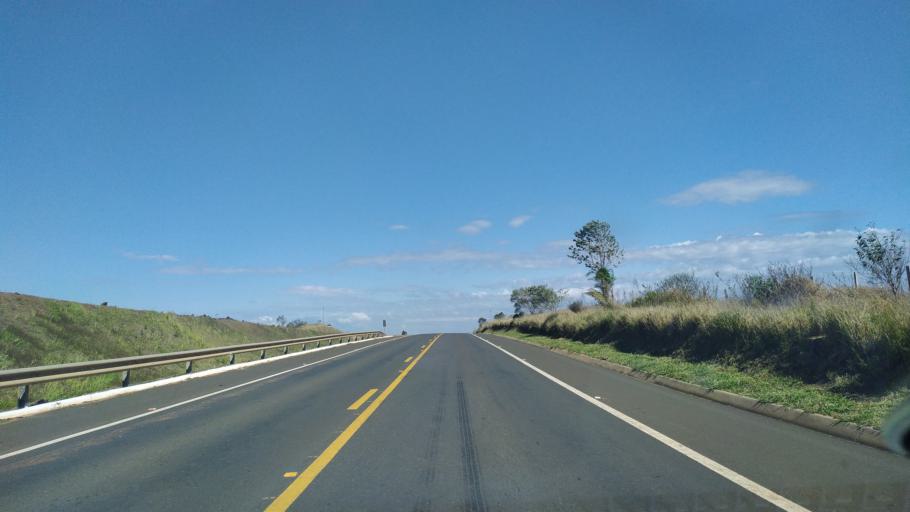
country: BR
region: Parana
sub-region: Ortigueira
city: Ortigueira
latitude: -24.2761
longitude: -50.8065
